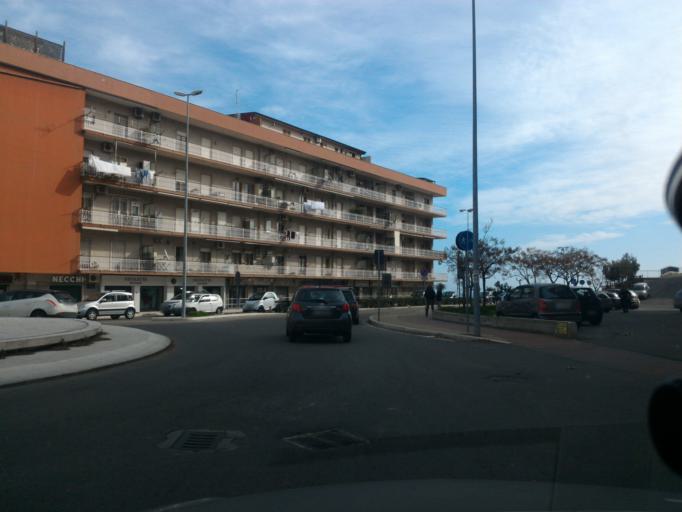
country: IT
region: Calabria
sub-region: Provincia di Crotone
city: Crotone
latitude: 39.0761
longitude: 17.1259
